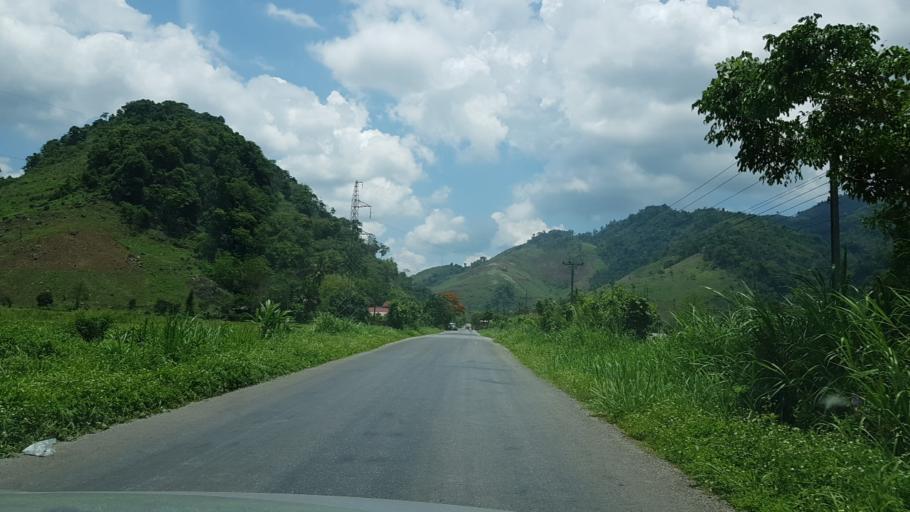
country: LA
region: Vientiane
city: Muang Kasi
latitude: 19.1308
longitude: 102.2745
